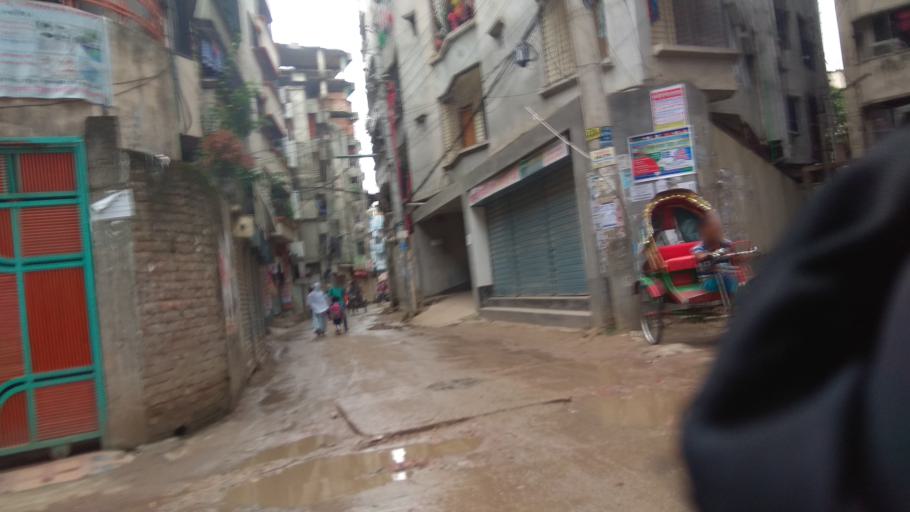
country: BD
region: Dhaka
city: Azimpur
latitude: 23.7969
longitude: 90.3589
